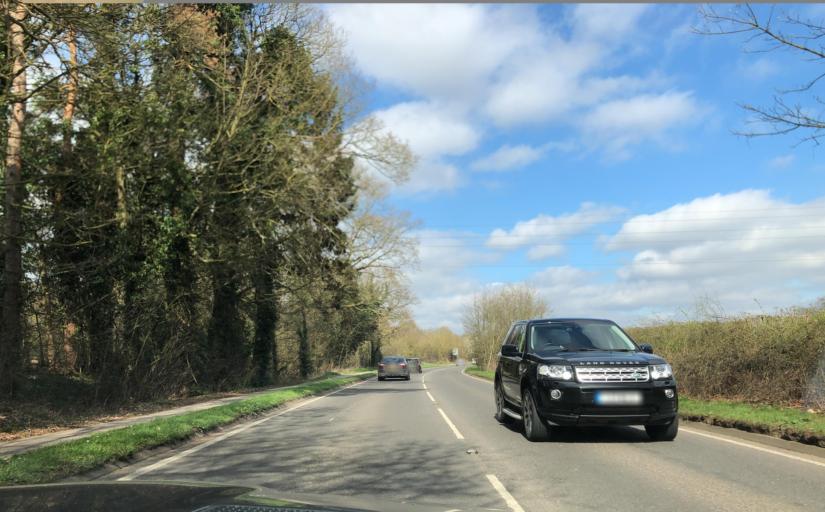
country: GB
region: England
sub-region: Warwickshire
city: Warwick
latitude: 52.3019
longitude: -1.5753
